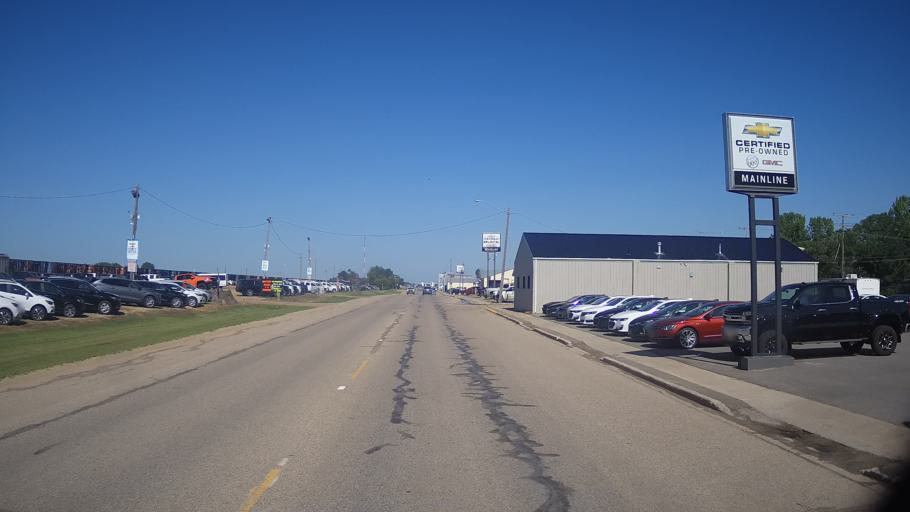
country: CA
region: Saskatchewan
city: Watrous
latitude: 51.6701
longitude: -105.4636
